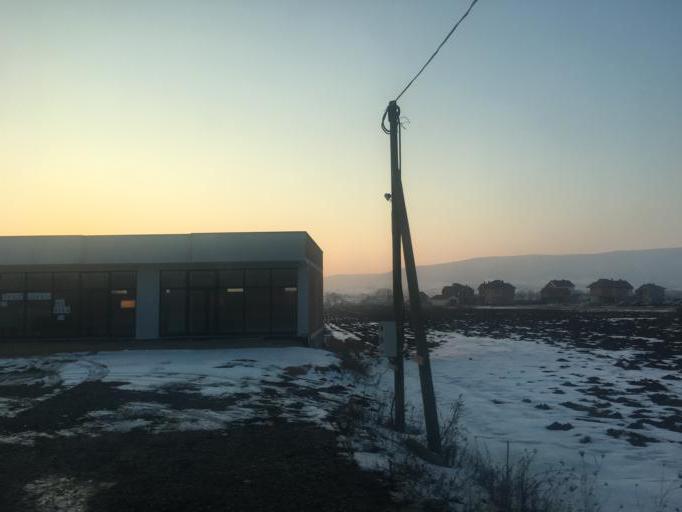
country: XK
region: Pristina
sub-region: Komuna e Drenasit
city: Glogovac
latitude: 42.5844
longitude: 20.8983
